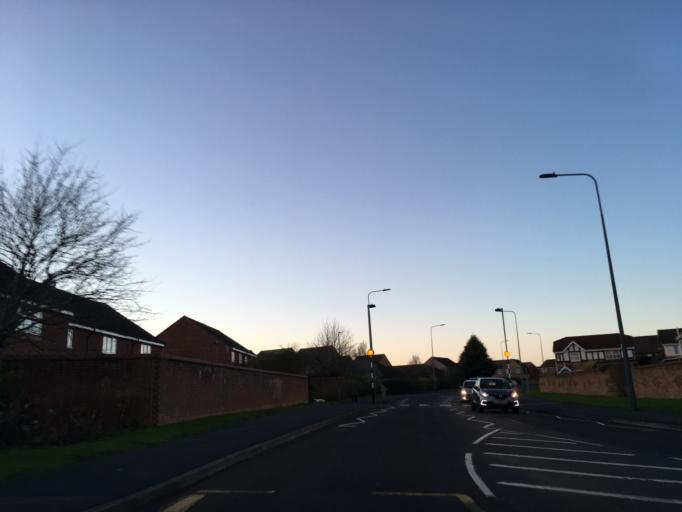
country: GB
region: England
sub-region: South Gloucestershire
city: Stoke Gifford
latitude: 51.5315
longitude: -2.5506
